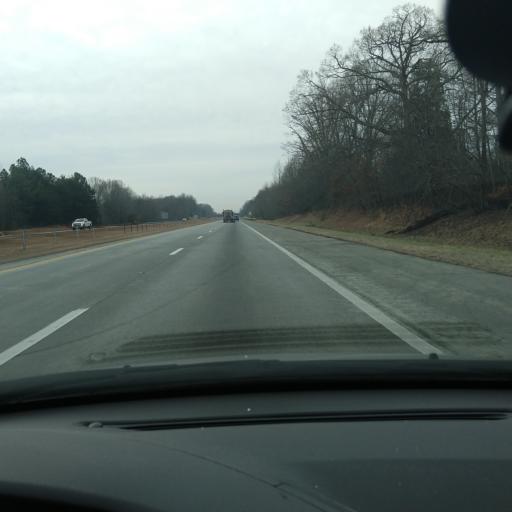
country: US
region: North Carolina
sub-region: Davidson County
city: Lexington
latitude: 35.8274
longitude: -80.2838
